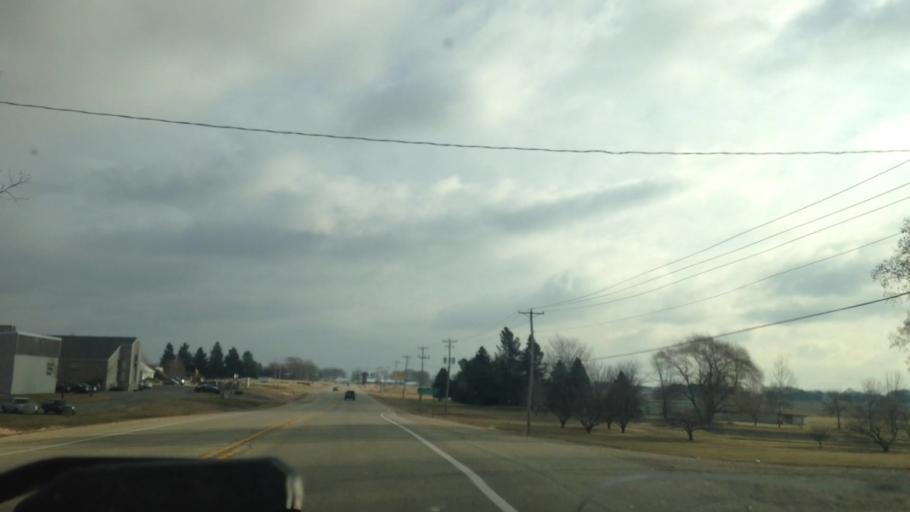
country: US
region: Wisconsin
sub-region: Dodge County
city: Beaver Dam
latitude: 43.4443
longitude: -88.7735
